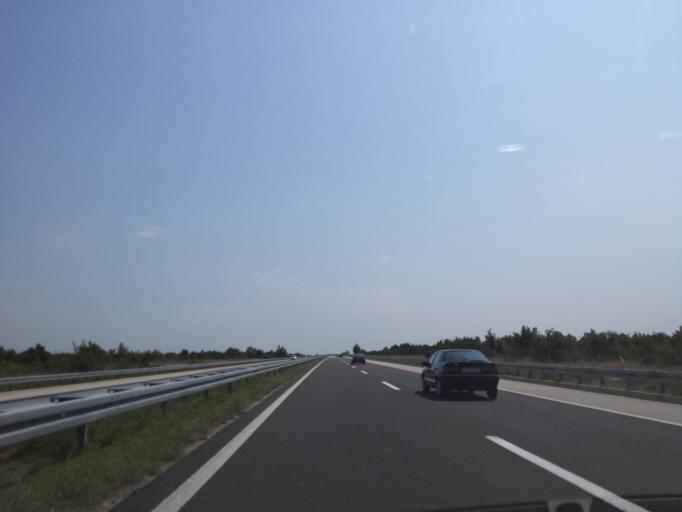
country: HR
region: Zadarska
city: Benkovac
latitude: 43.9827
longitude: 15.6340
